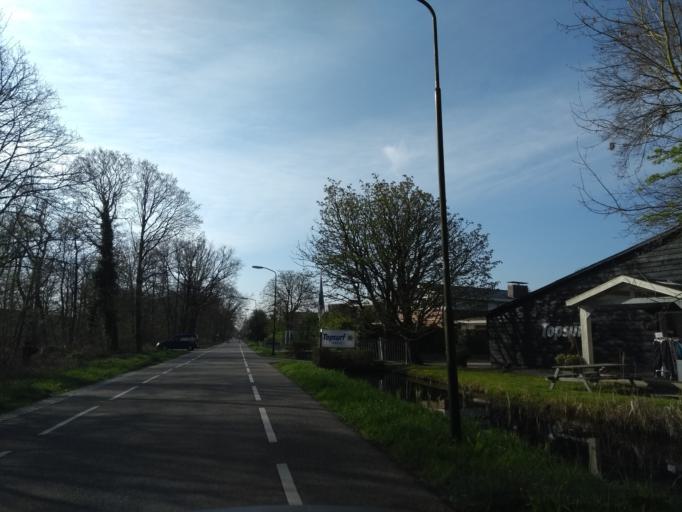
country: NL
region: North Holland
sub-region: Gemeente Amsterdam
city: Amsterdam-Zuidoost
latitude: 52.2459
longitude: 4.9695
